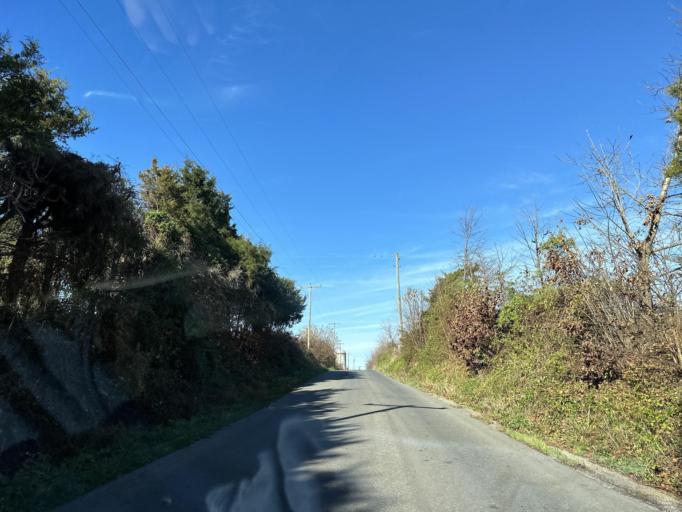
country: US
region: Virginia
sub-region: Augusta County
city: Weyers Cave
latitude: 38.2187
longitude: -78.9193
